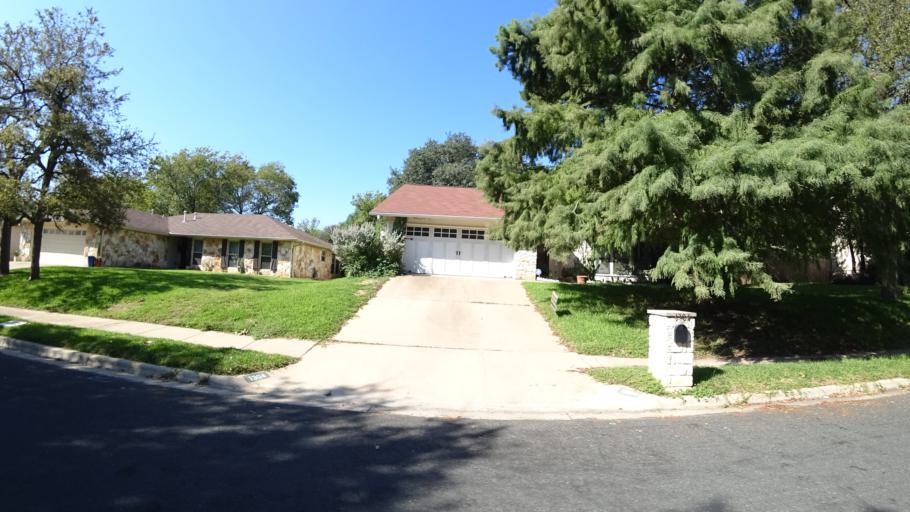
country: US
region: Texas
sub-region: Travis County
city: Rollingwood
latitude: 30.2718
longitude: -97.8062
